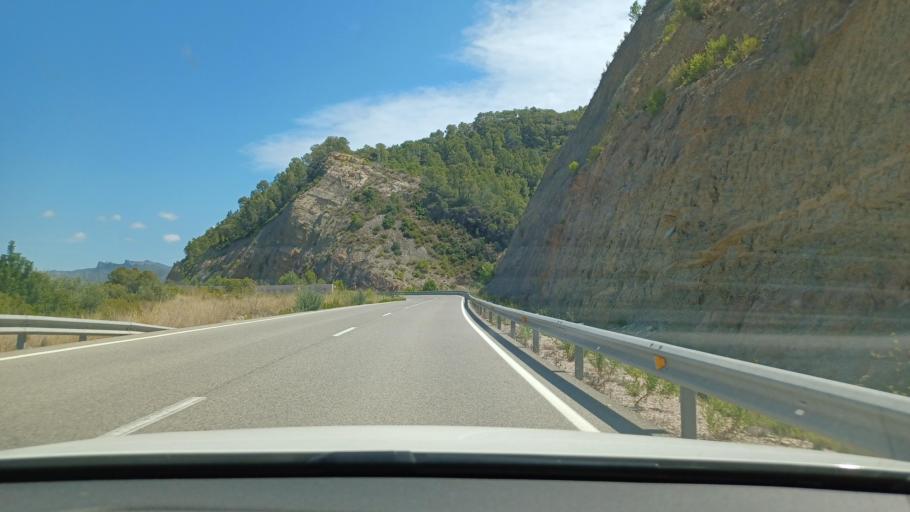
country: ES
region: Catalonia
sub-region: Provincia de Tarragona
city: Benifallet
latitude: 40.9516
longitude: 0.4504
